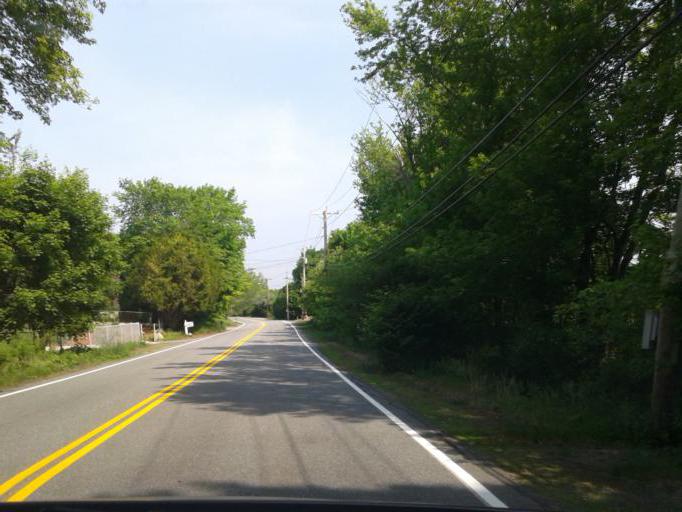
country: US
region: Massachusetts
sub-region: Worcester County
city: Westborough
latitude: 42.2556
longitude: -71.6048
